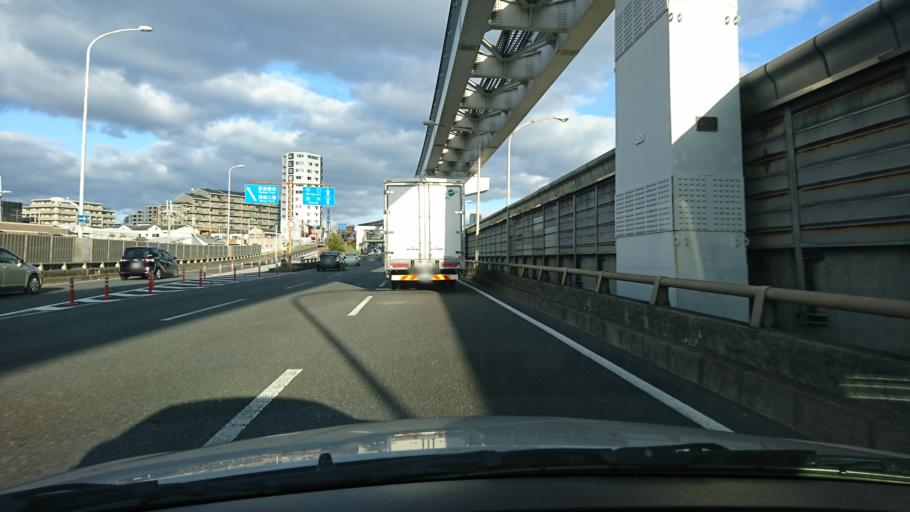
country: JP
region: Osaka
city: Toyonaka
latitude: 34.8007
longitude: 135.4682
